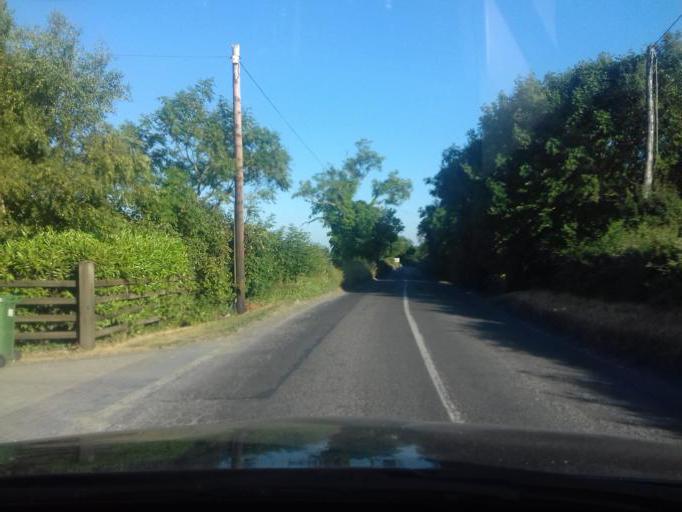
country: IE
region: Leinster
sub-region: Dublin City
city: Finglas
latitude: 53.4434
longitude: -6.3013
